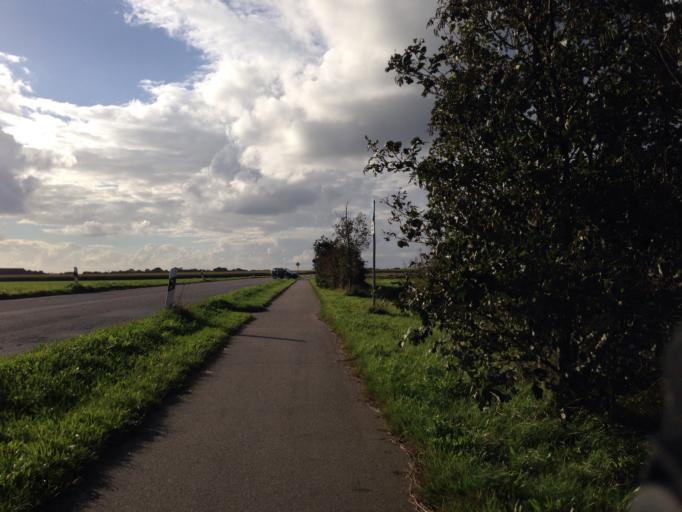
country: DE
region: Schleswig-Holstein
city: Oldsum
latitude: 54.7255
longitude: 8.4625
